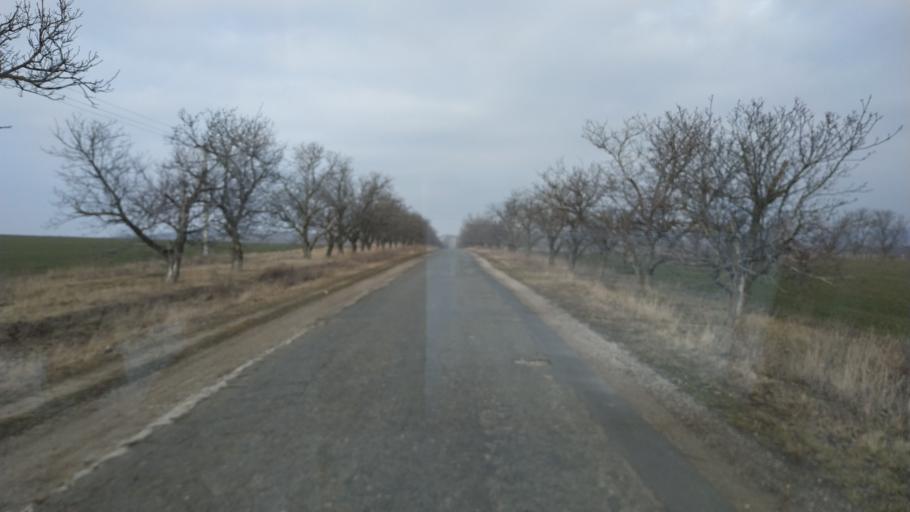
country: MD
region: Hincesti
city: Dancu
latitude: 46.8670
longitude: 28.2930
